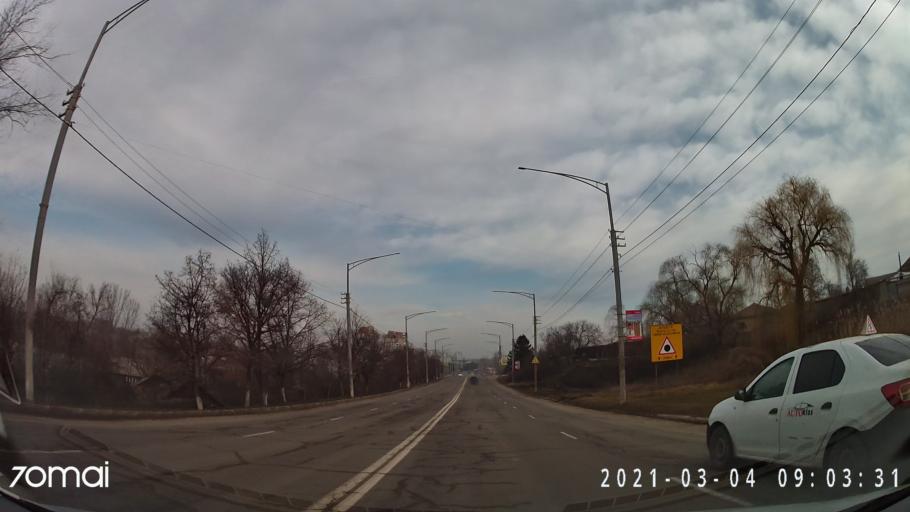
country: MD
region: Balti
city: Balti
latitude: 47.7504
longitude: 27.9440
